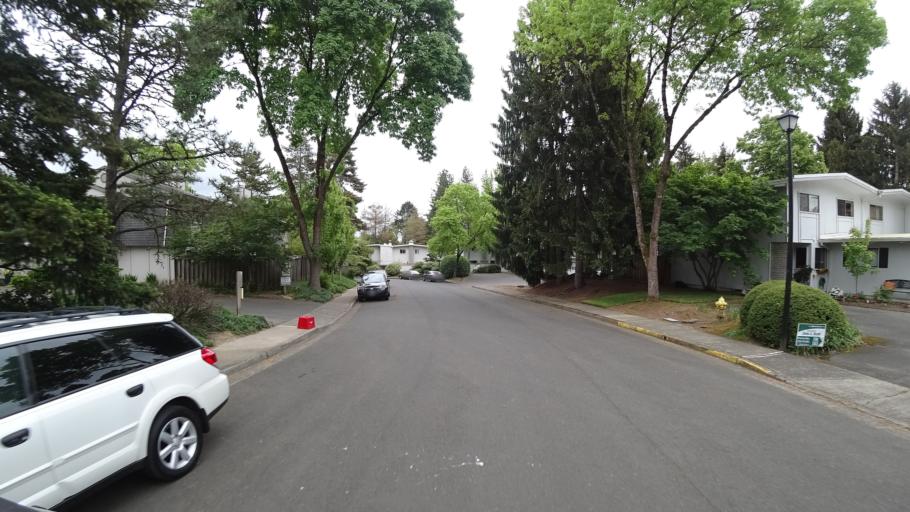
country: US
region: Oregon
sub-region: Washington County
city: Beaverton
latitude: 45.4698
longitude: -122.8020
